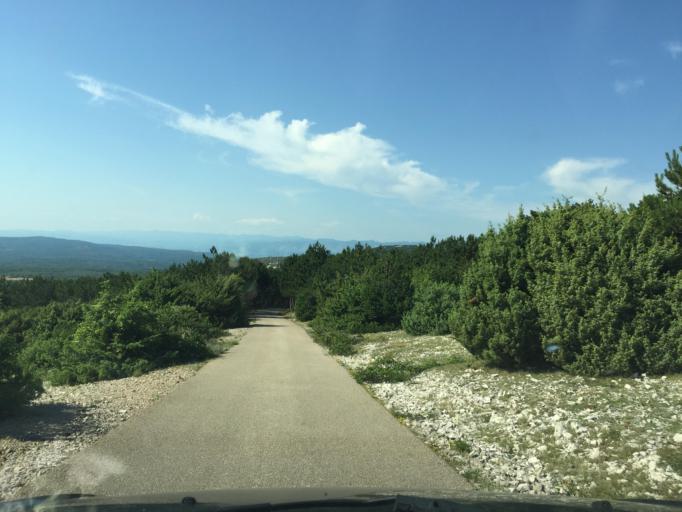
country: HR
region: Primorsko-Goranska
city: Punat
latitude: 45.0200
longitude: 14.6736
